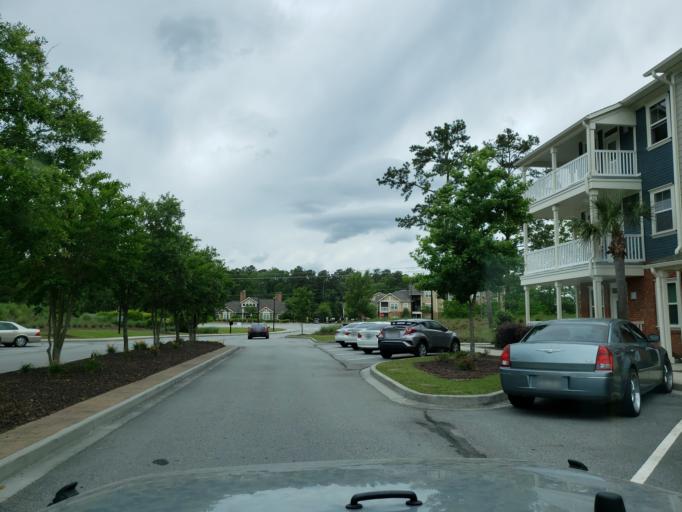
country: US
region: Georgia
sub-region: Chatham County
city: Pooler
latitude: 32.1750
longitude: -81.2307
